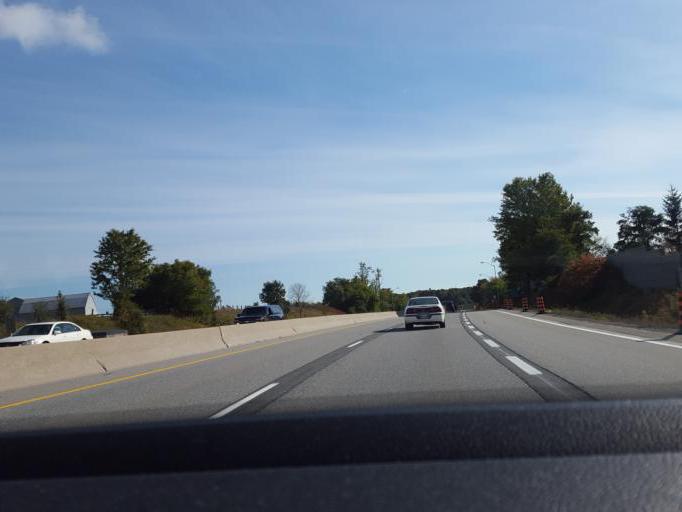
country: CA
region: Ontario
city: Oshawa
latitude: 43.9762
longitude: -78.6112
